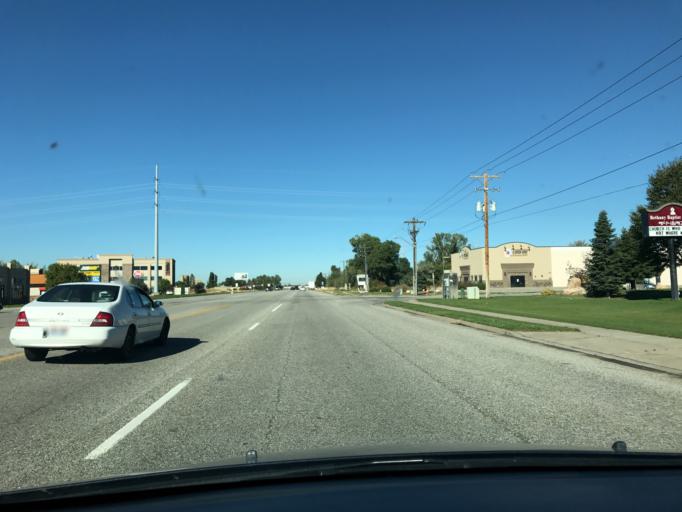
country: US
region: Utah
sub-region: Davis County
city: South Weber
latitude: 41.1018
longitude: -111.9439
